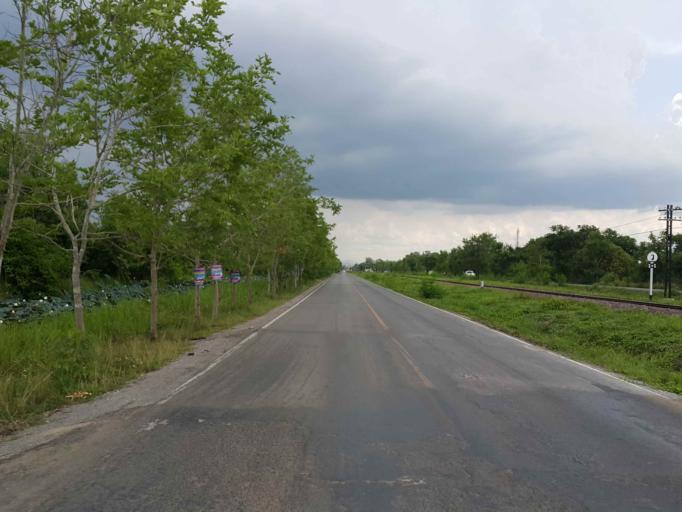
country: TH
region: Chiang Mai
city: Saraphi
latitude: 18.7228
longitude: 99.0365
